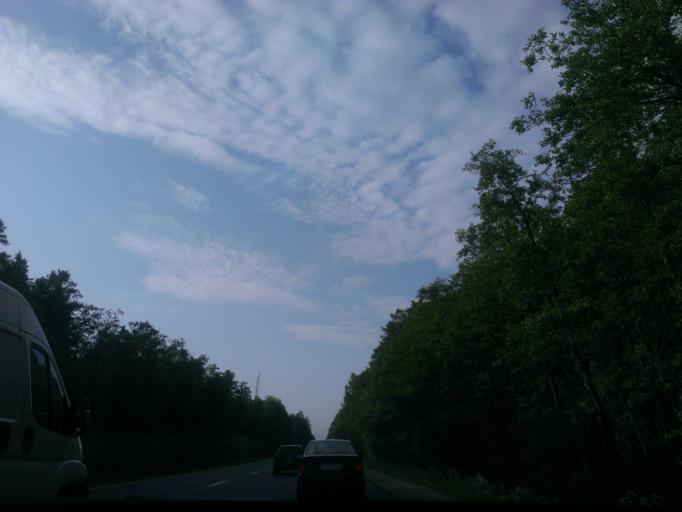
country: LV
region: Kekava
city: Kekava
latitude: 56.7406
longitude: 24.2521
